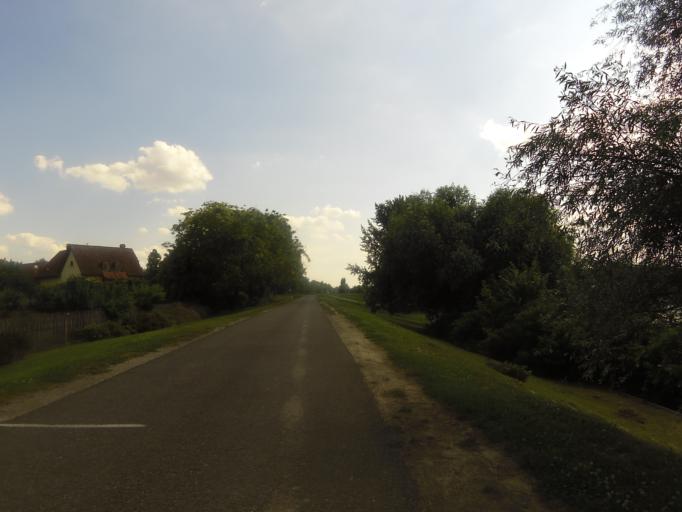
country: HU
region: Jasz-Nagykun-Szolnok
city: Tiszafured
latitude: 47.6102
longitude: 20.7230
